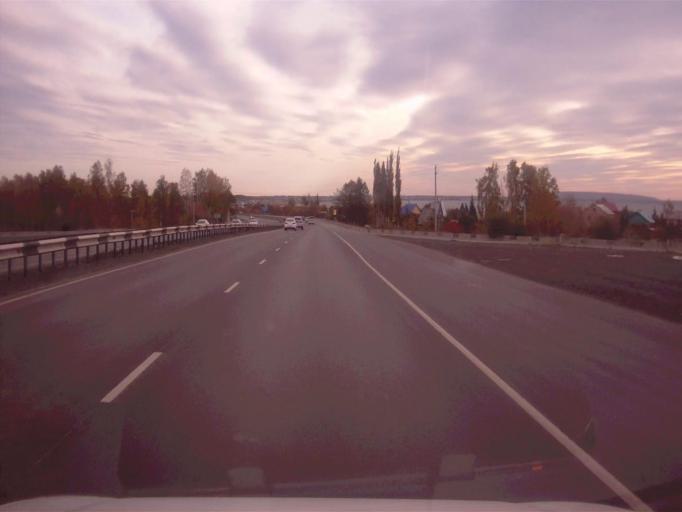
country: RU
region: Chelyabinsk
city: Novosineglazovskiy
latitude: 55.0378
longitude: 61.4413
